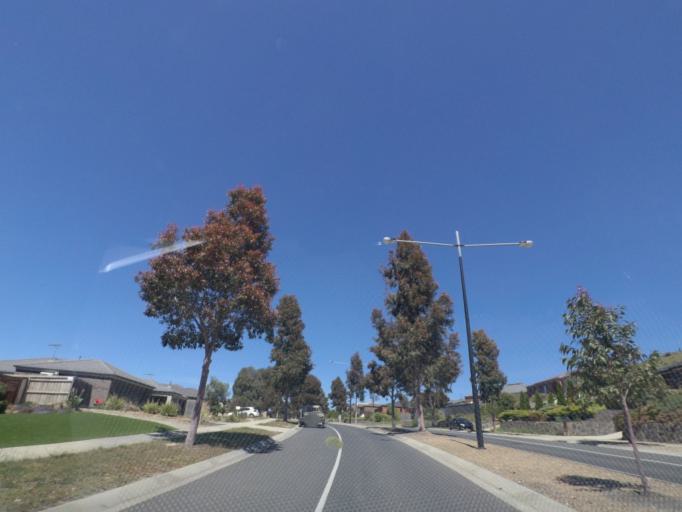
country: AU
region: Victoria
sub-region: Hume
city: Sunbury
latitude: -37.5640
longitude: 144.6987
